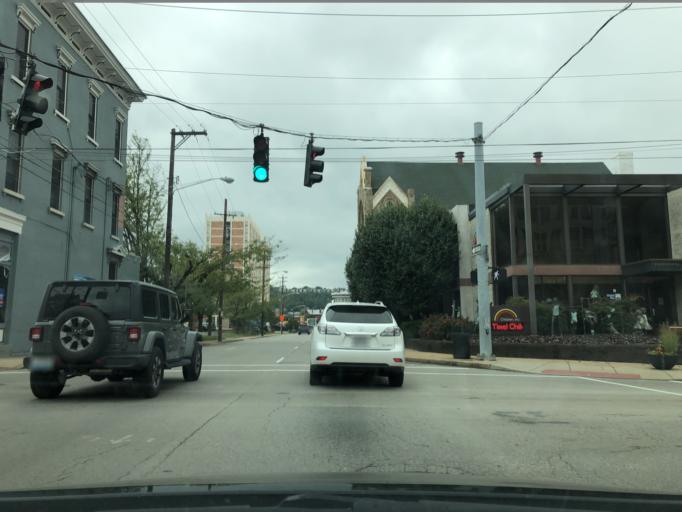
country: US
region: Kentucky
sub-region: Kenton County
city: Covington
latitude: 39.0871
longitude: -84.5109
